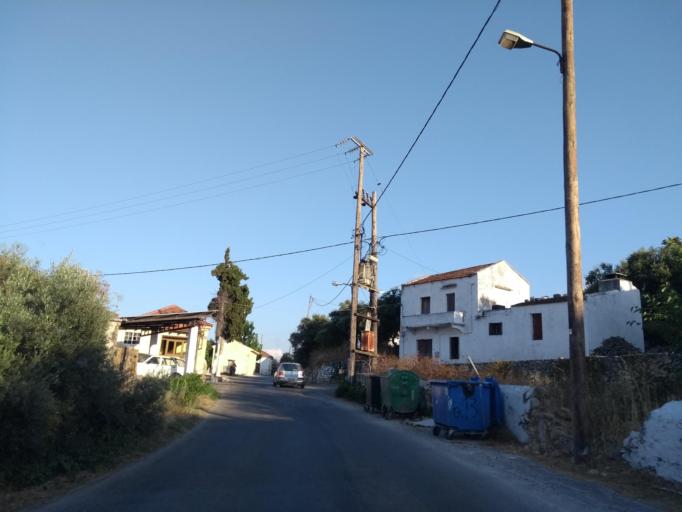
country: GR
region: Crete
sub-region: Nomos Chanias
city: Kalivai
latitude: 35.4348
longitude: 24.1792
